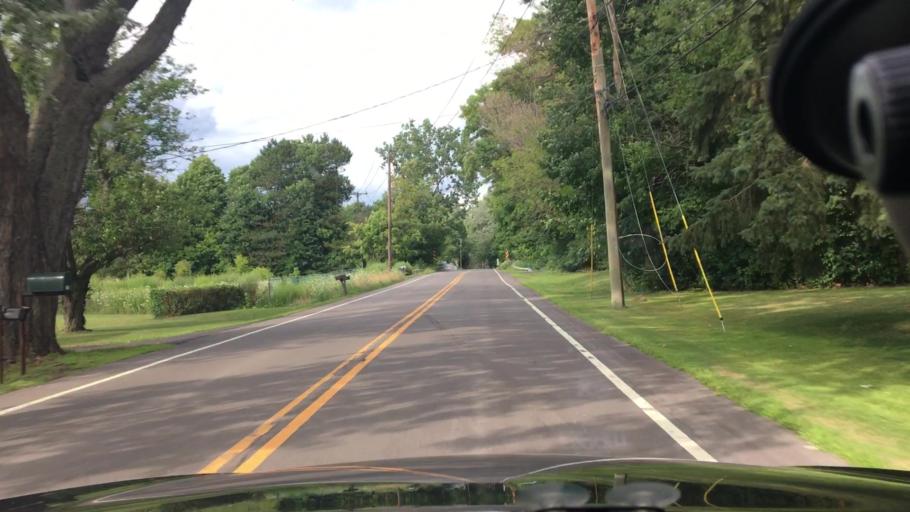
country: US
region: New York
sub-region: Erie County
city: Elma Center
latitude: 42.8192
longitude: -78.6655
